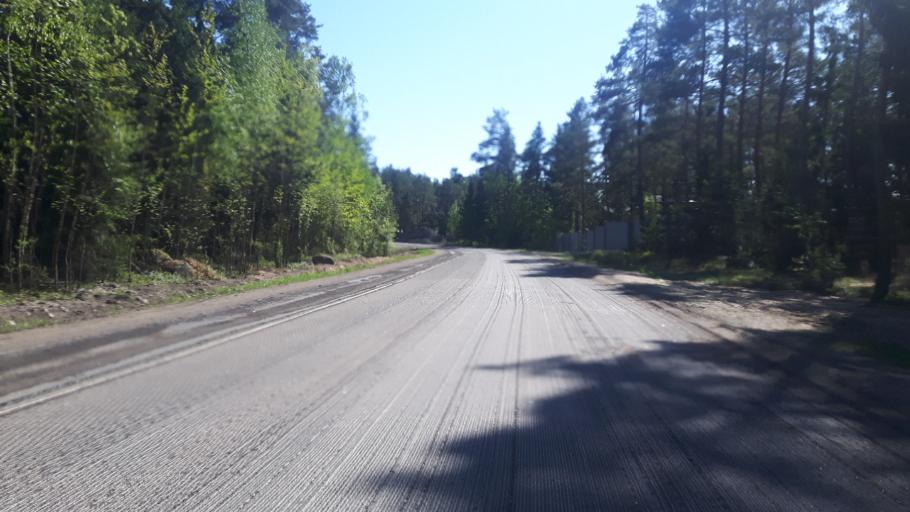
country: RU
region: Leningrad
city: Sosnovyy Bor
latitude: 60.2351
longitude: 29.0013
